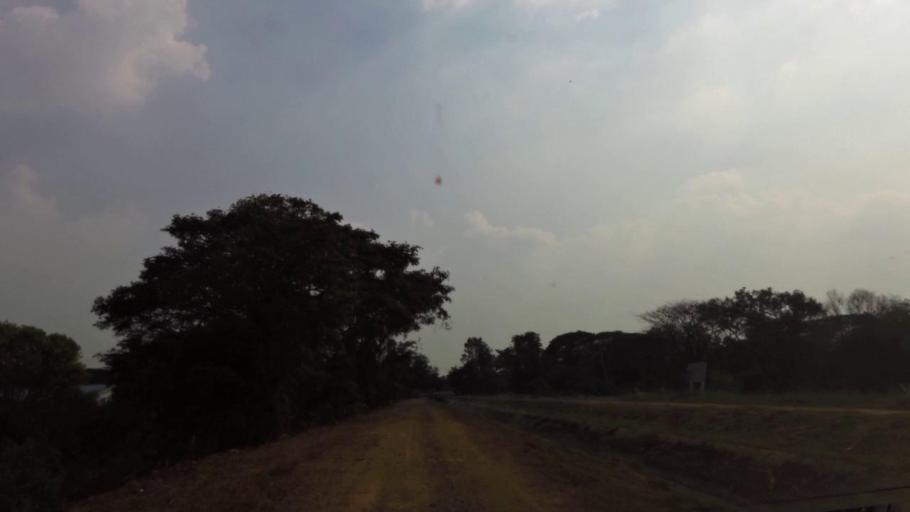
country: TH
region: Phra Nakhon Si Ayutthaya
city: Phra Nakhon Si Ayutthaya
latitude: 14.3119
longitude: 100.5628
